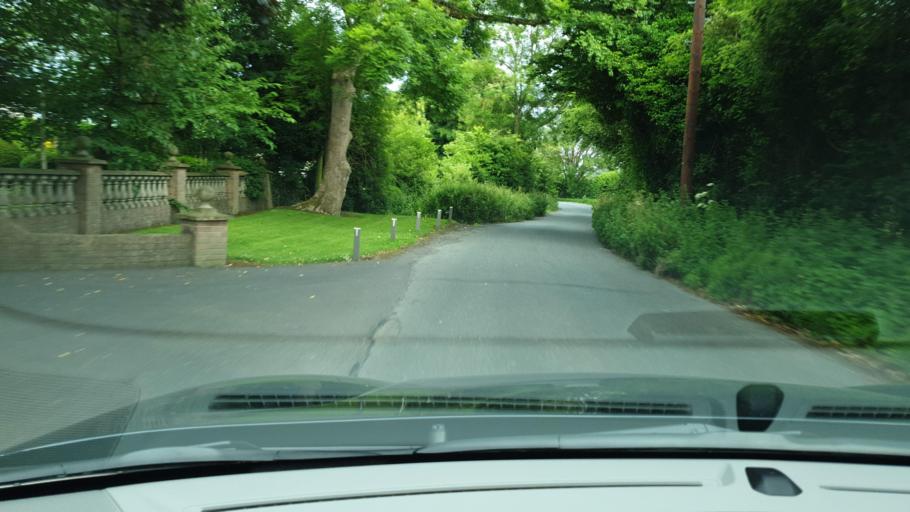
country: IE
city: Confey
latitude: 53.3933
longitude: -6.4968
